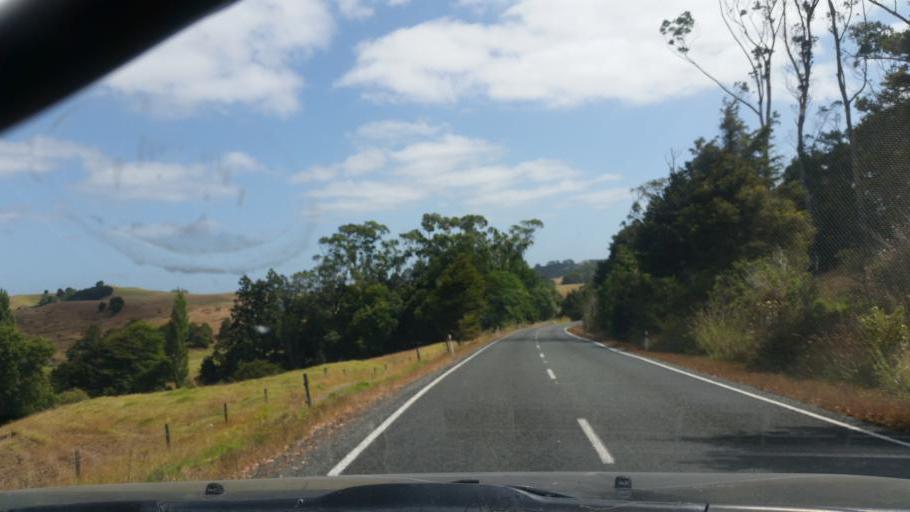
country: NZ
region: Northland
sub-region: Whangarei
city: Ruakaka
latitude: -35.9459
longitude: 174.2922
